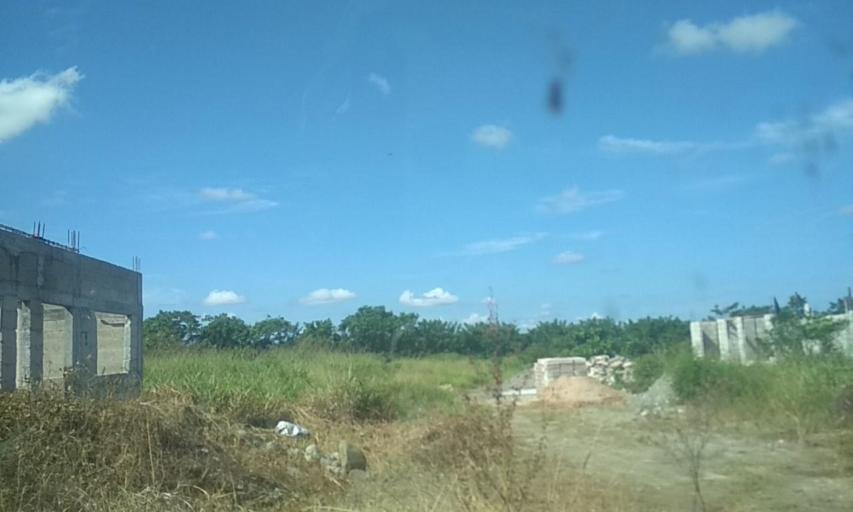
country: MX
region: Veracruz
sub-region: Martinez de la Torre
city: La Union Paso Largo
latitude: 20.1347
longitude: -96.9906
